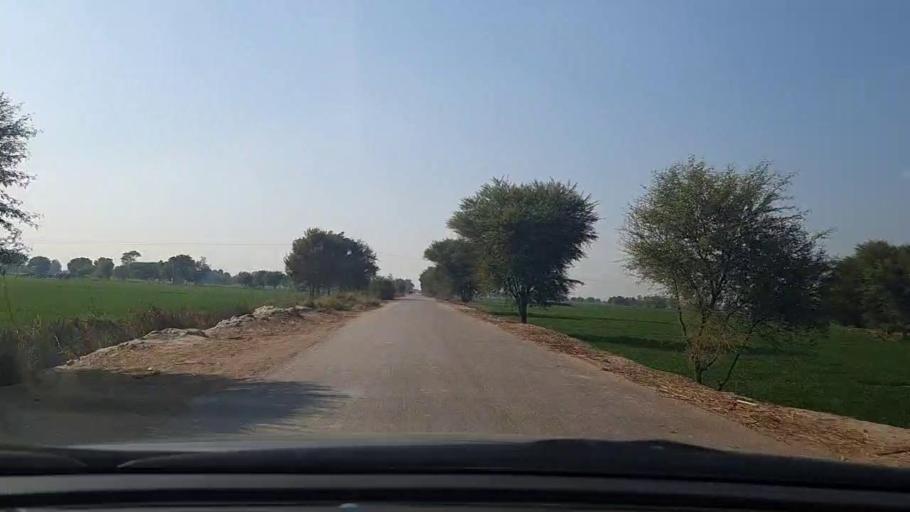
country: PK
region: Sindh
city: Daulatpur
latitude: 26.3160
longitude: 68.0635
